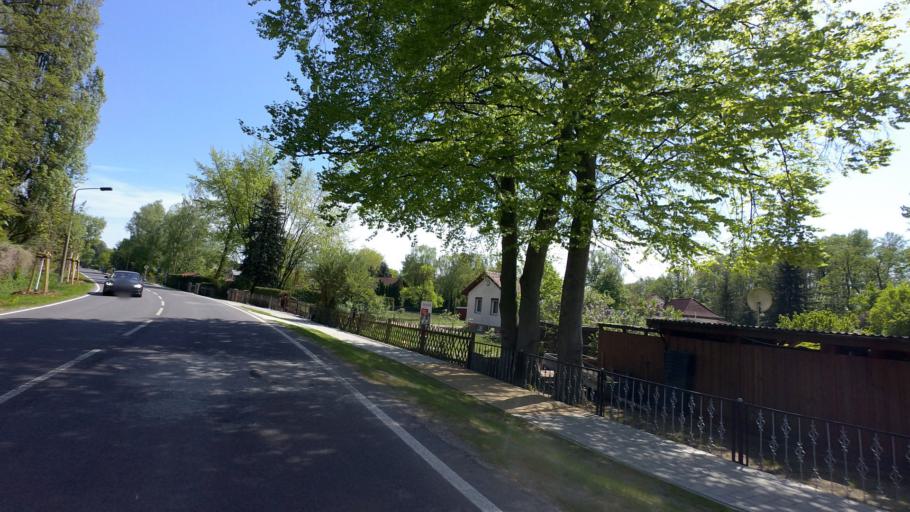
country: DE
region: Brandenburg
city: Bestensee
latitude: 52.2572
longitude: 13.6392
